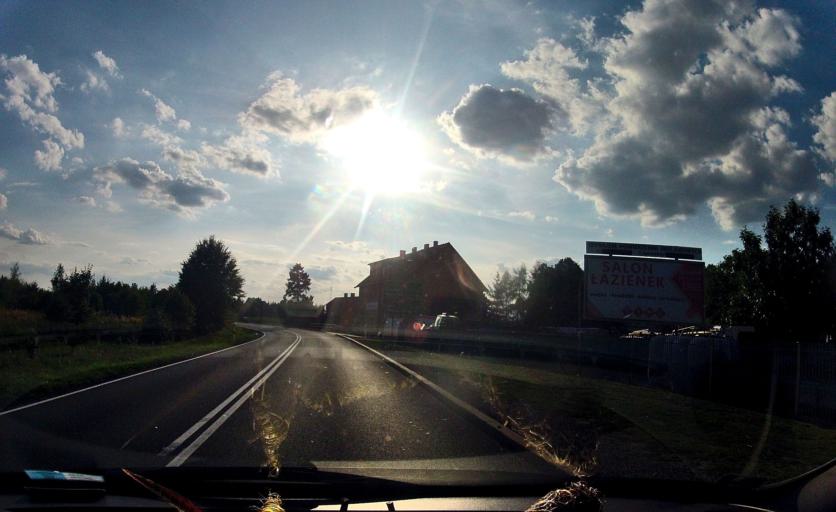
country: PL
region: Opole Voivodeship
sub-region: Powiat oleski
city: Praszka
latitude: 51.0562
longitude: 18.4392
